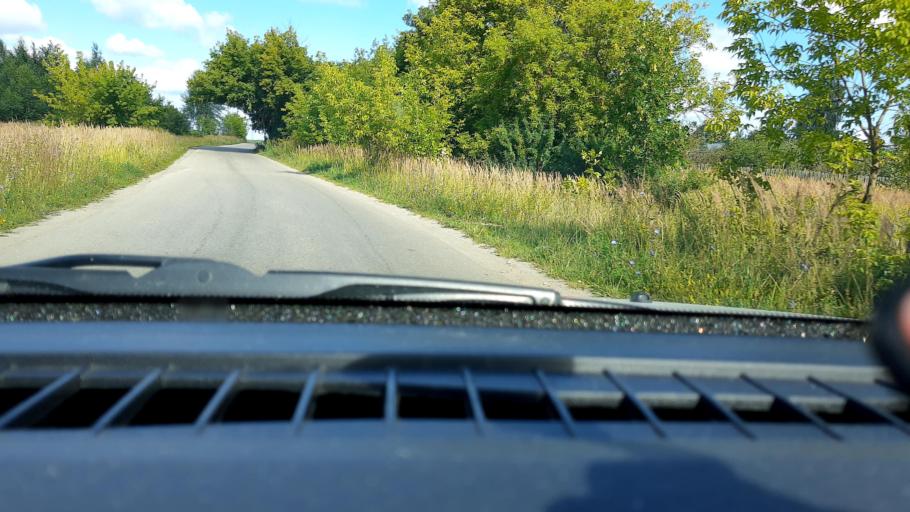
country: RU
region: Nizjnij Novgorod
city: Gorbatovka
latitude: 56.2653
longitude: 43.7278
